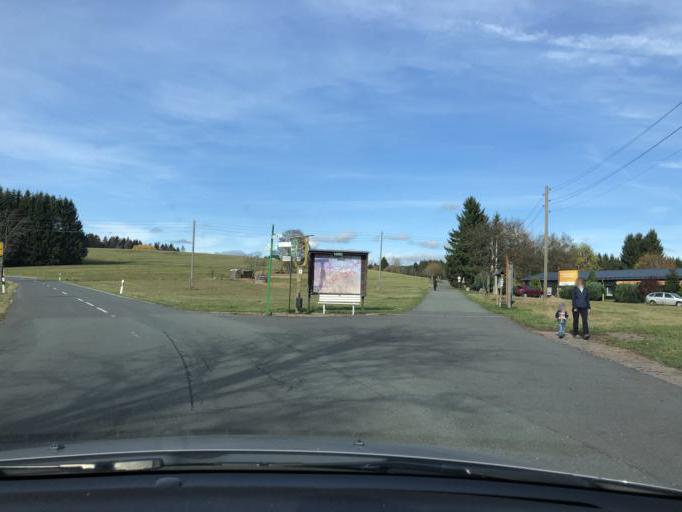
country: DE
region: Thuringia
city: Masserberg
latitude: 50.5078
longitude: 10.9322
